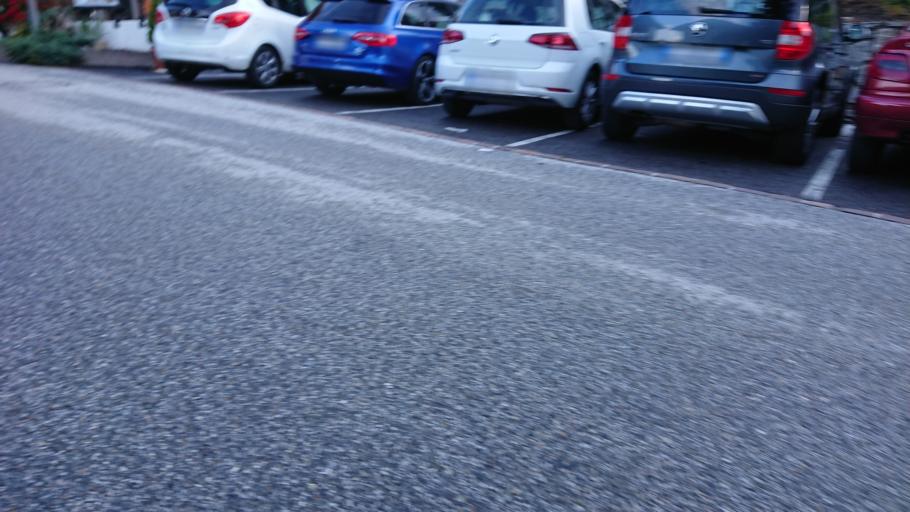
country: IT
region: Trentino-Alto Adige
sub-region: Bolzano
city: Campo di Trens
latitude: 46.8757
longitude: 11.4861
